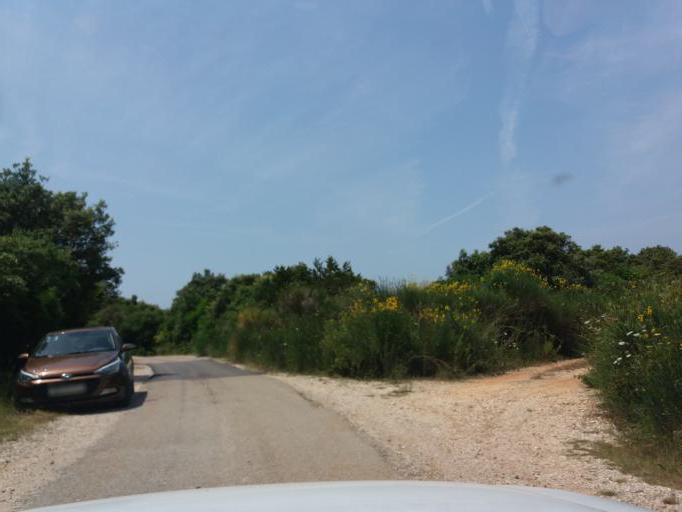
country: HR
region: Zadarska
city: Ugljan
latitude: 44.1493
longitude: 14.8299
